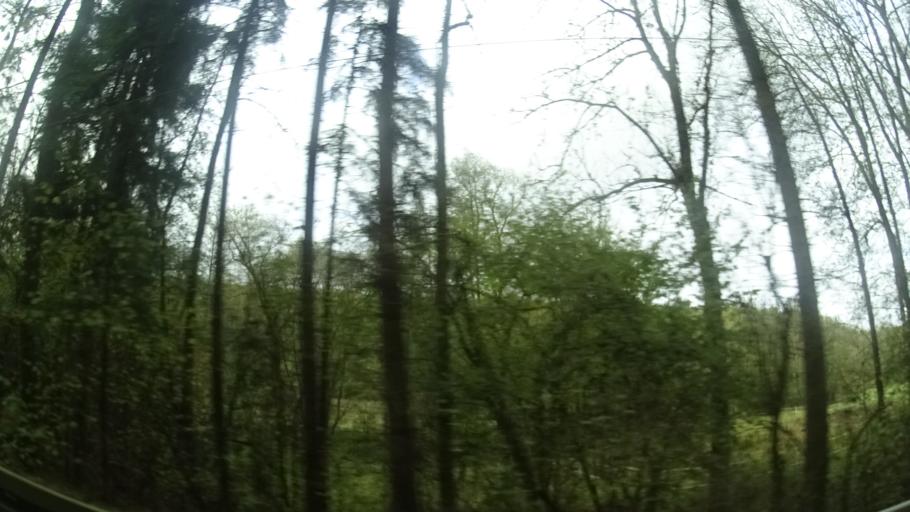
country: DE
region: Bavaria
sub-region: Regierungsbezirk Unterfranken
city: Aubstadt
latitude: 50.3437
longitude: 10.4099
